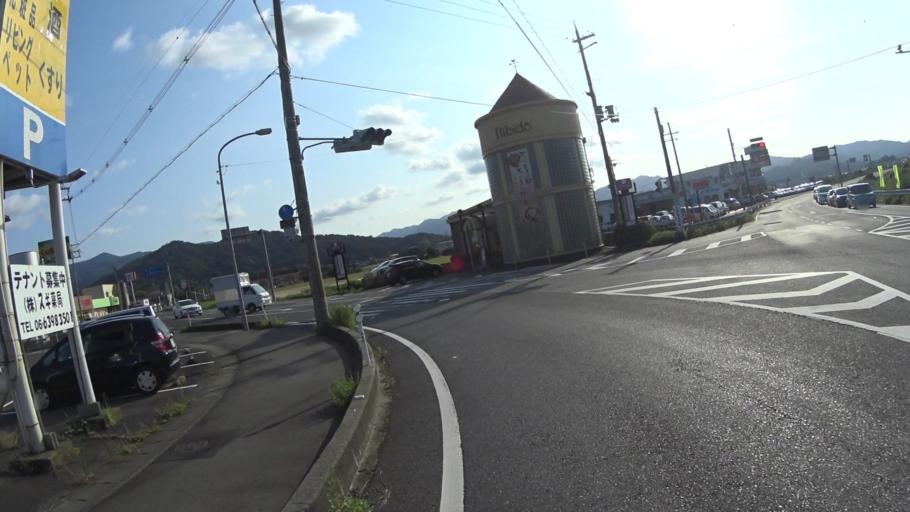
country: JP
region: Kyoto
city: Miyazu
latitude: 35.5350
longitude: 135.1226
